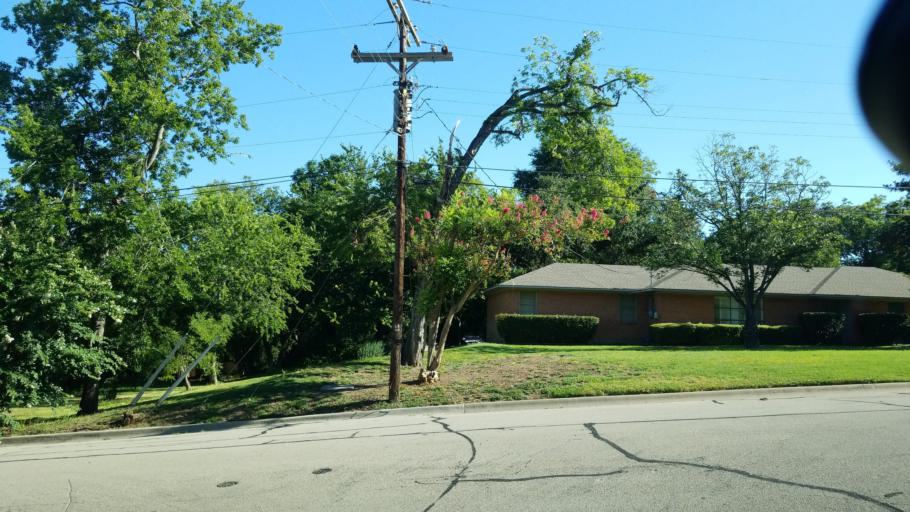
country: US
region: Texas
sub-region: Dallas County
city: Carrollton
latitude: 32.9518
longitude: -96.9021
